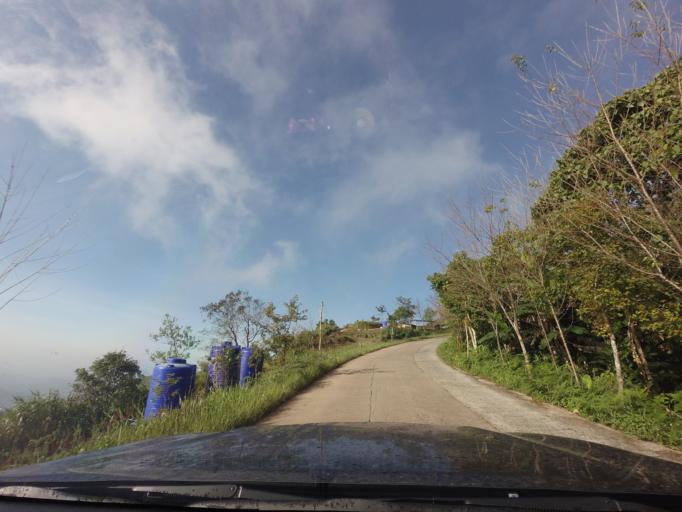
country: TH
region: Phetchabun
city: Lom Kao
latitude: 16.8939
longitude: 101.1037
